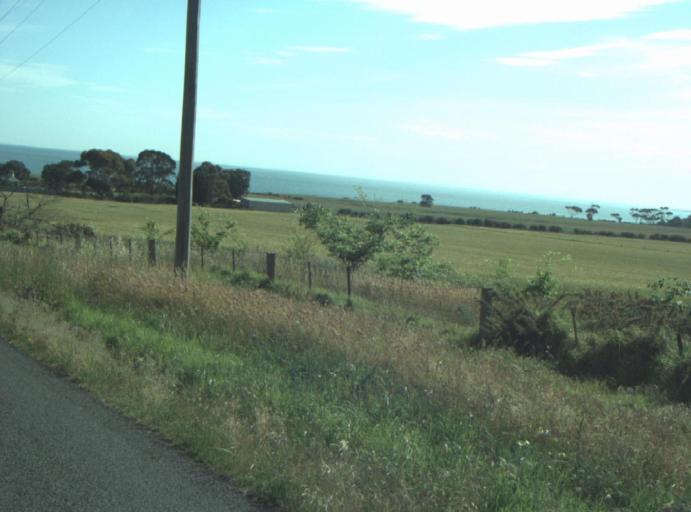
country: AU
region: Victoria
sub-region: Greater Geelong
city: Clifton Springs
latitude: -38.1665
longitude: 144.5159
